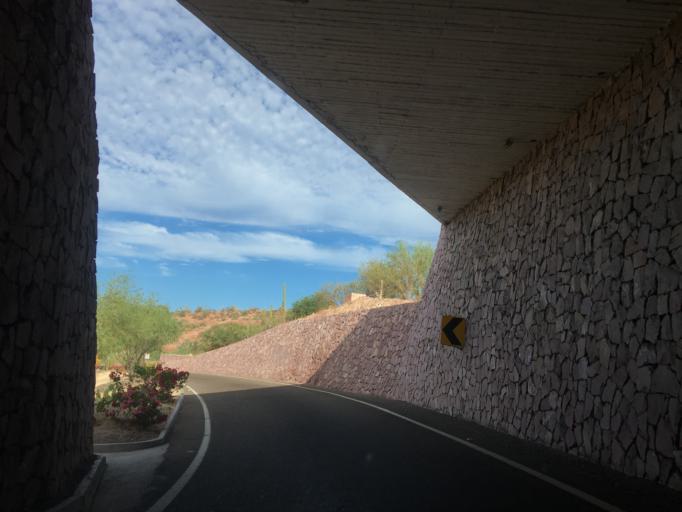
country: MX
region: Baja California Sur
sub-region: La Paz
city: La Paz
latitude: 24.2141
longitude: -110.2947
